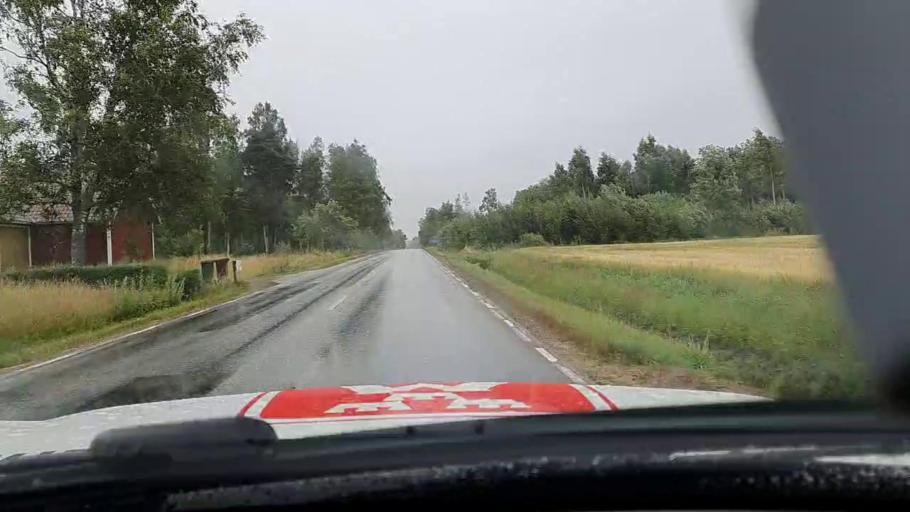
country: SE
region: Vaestra Goetaland
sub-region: Toreboda Kommun
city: Toereboda
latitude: 58.7002
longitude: 14.1346
